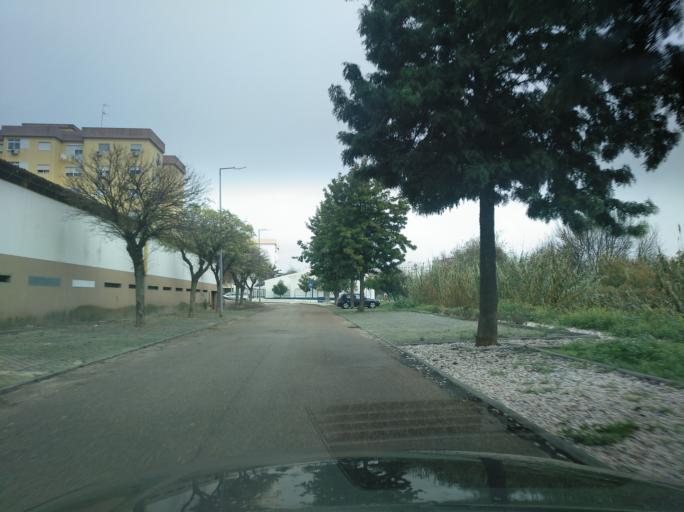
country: PT
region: Portalegre
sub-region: Elvas
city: Elvas
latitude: 38.8677
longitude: -7.1706
